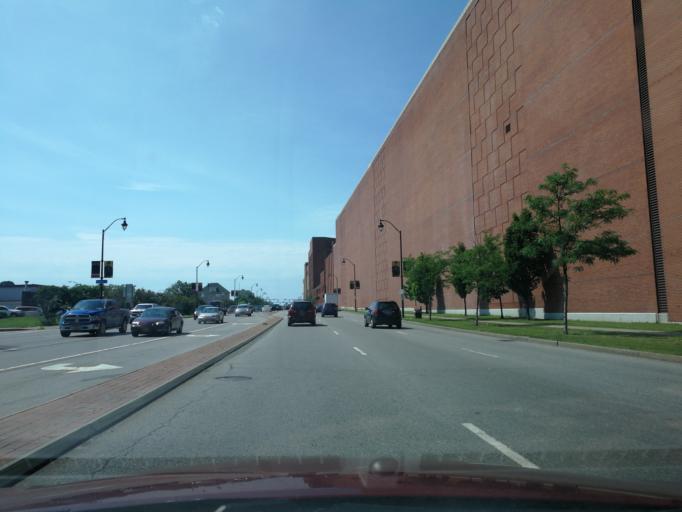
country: US
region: New York
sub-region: Monroe County
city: Rochester
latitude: 43.1950
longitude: -77.6290
